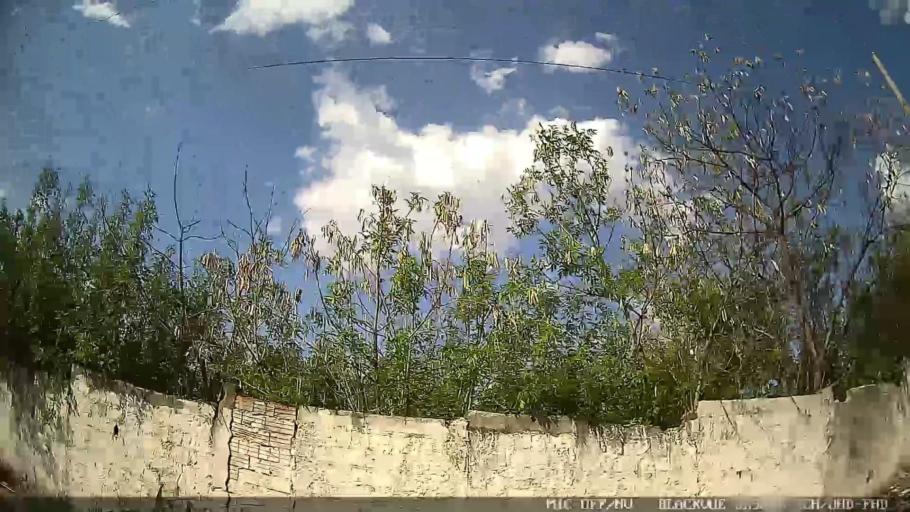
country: BR
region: Sao Paulo
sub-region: Ferraz De Vasconcelos
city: Ferraz de Vasconcelos
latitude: -23.5271
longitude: -46.4255
